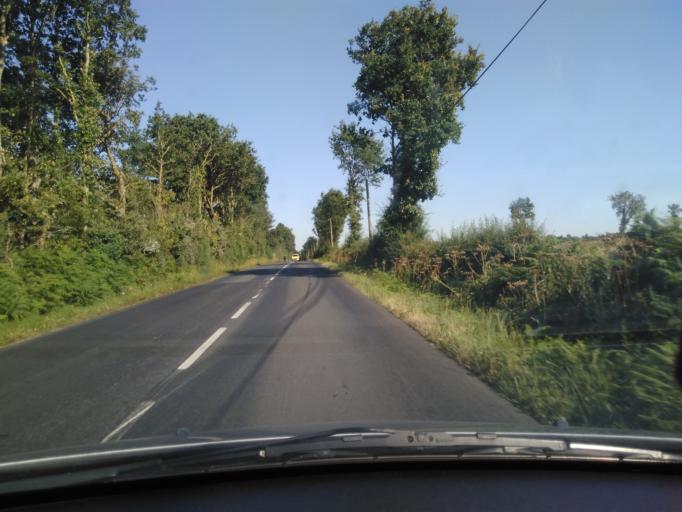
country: FR
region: Pays de la Loire
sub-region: Departement de la Vendee
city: Dompierre-sur-Yon
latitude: 46.7307
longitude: -1.3656
